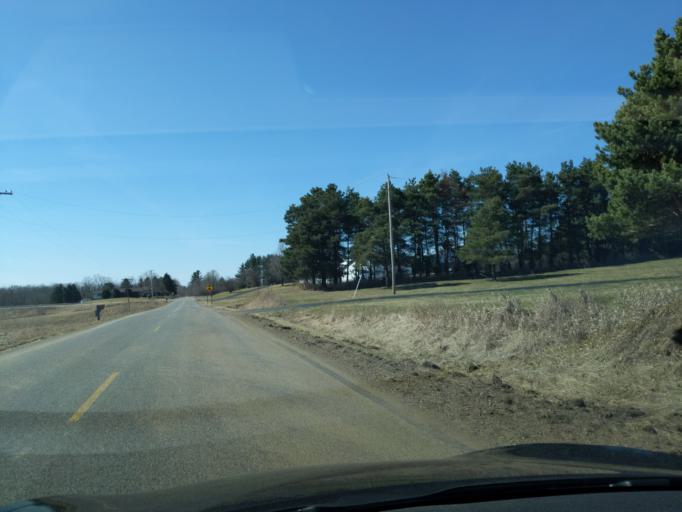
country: US
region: Michigan
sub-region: Ionia County
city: Lake Odessa
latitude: 42.7126
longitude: -85.0918
